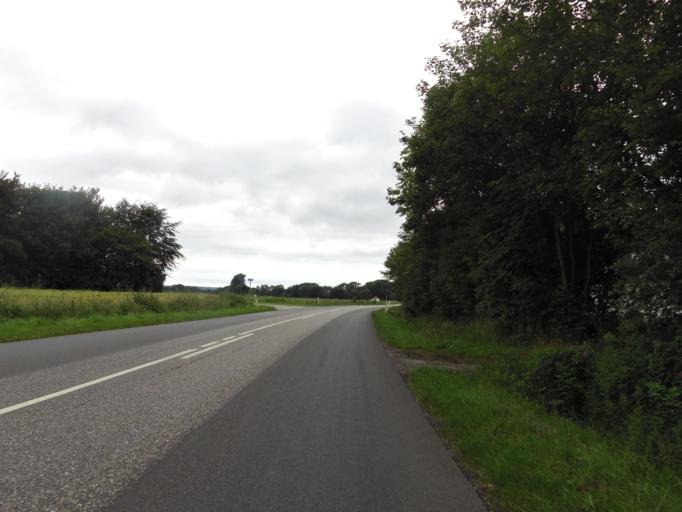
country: DK
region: South Denmark
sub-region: Tonder Kommune
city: Toftlund
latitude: 55.1487
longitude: 9.0431
